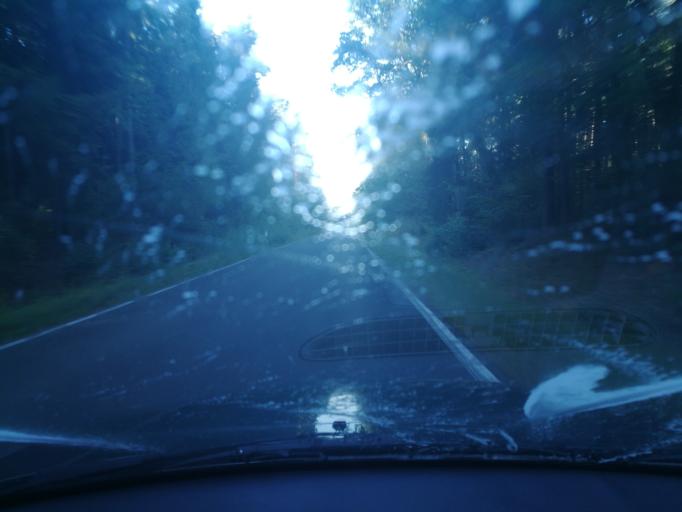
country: DE
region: Bavaria
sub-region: Regierungsbezirk Mittelfranken
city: Hessdorf
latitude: 49.6118
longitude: 10.9379
